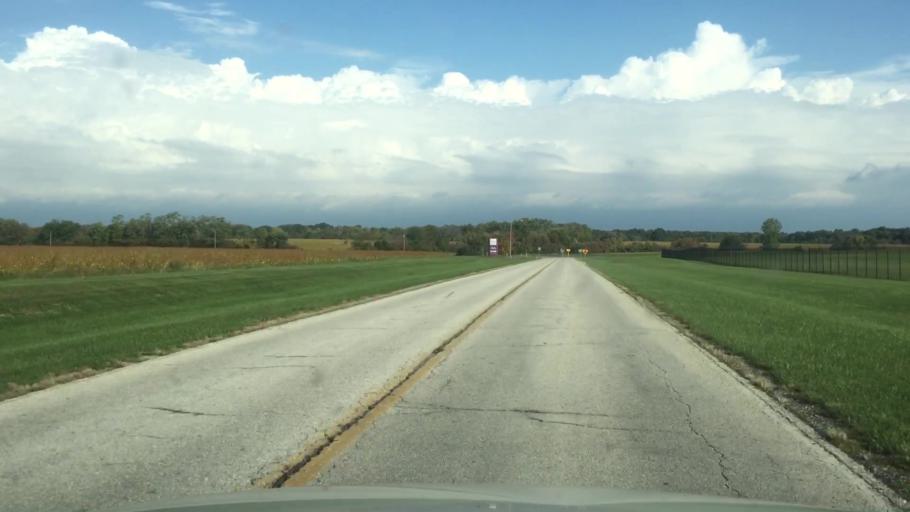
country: US
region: Missouri
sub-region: Boone County
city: Ashland
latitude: 38.8292
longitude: -92.2273
